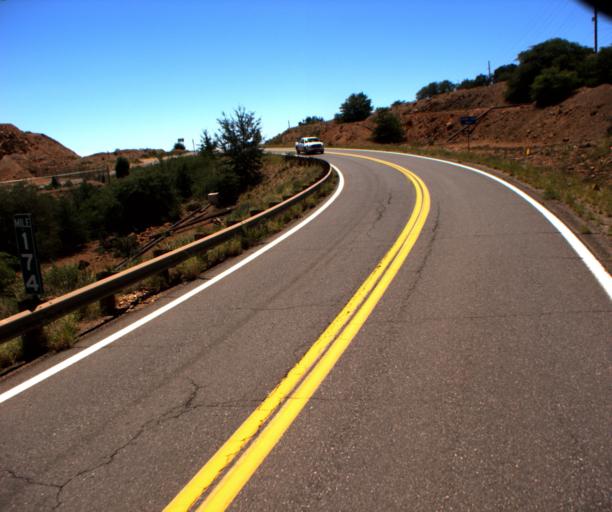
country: US
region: Arizona
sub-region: Greenlee County
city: Morenci
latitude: 33.0905
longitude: -109.3813
